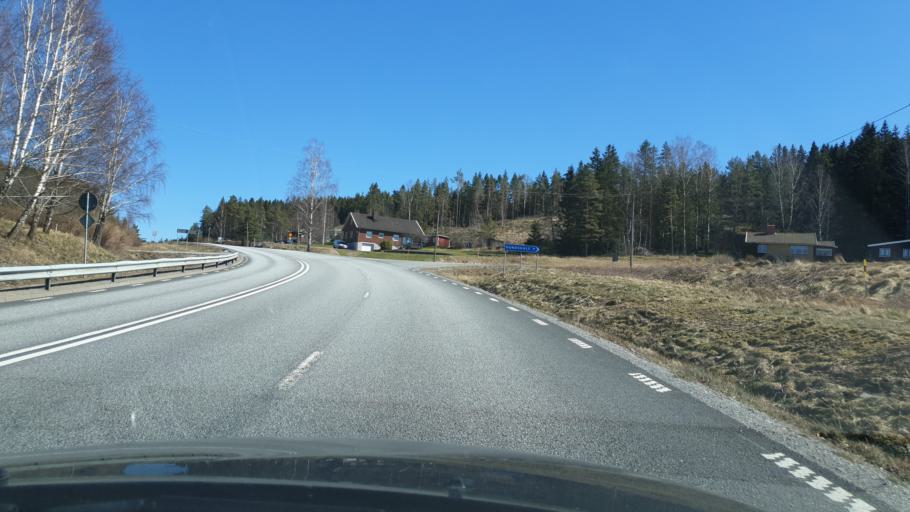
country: SE
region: Vaestra Goetaland
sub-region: Tanums Kommun
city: Tanumshede
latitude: 58.7939
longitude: 11.5783
